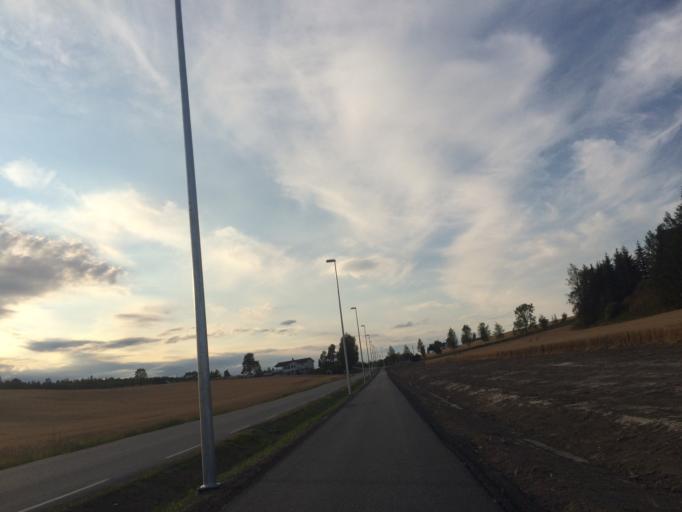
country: NO
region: Akershus
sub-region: Ski
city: Ski
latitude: 59.6875
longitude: 10.8671
